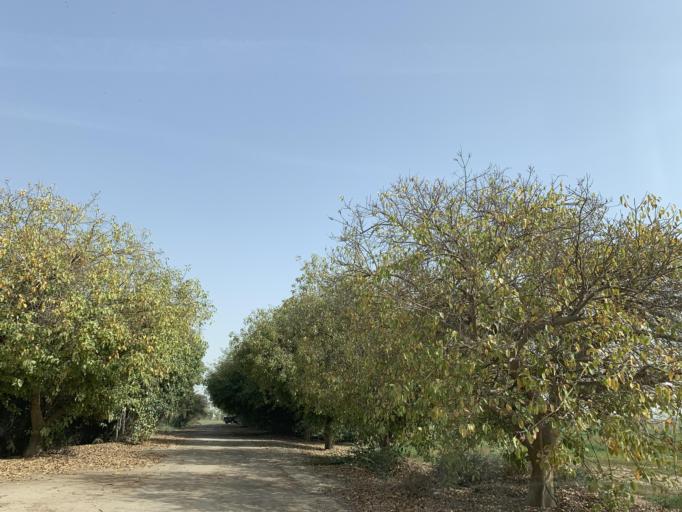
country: BH
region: Northern
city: Madinat `Isa
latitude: 26.1673
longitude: 50.5295
